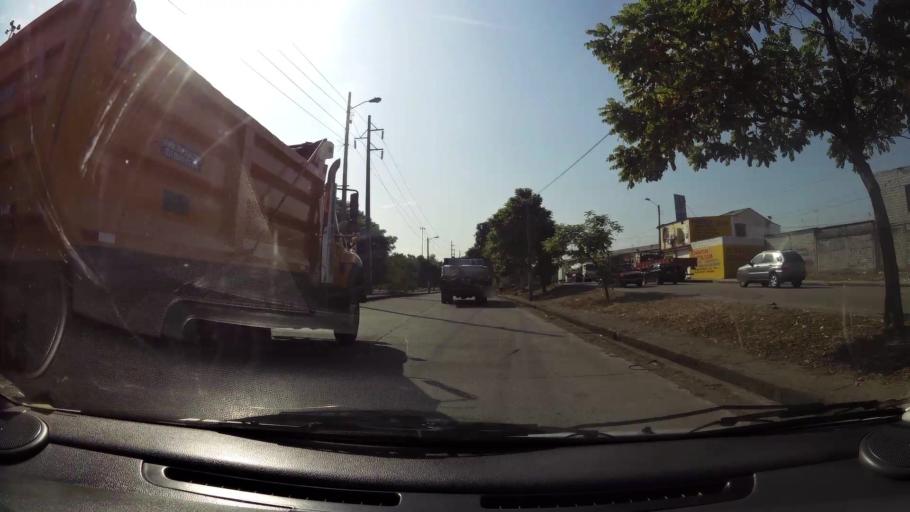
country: EC
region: Guayas
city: Eloy Alfaro
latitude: -2.0770
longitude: -79.9191
